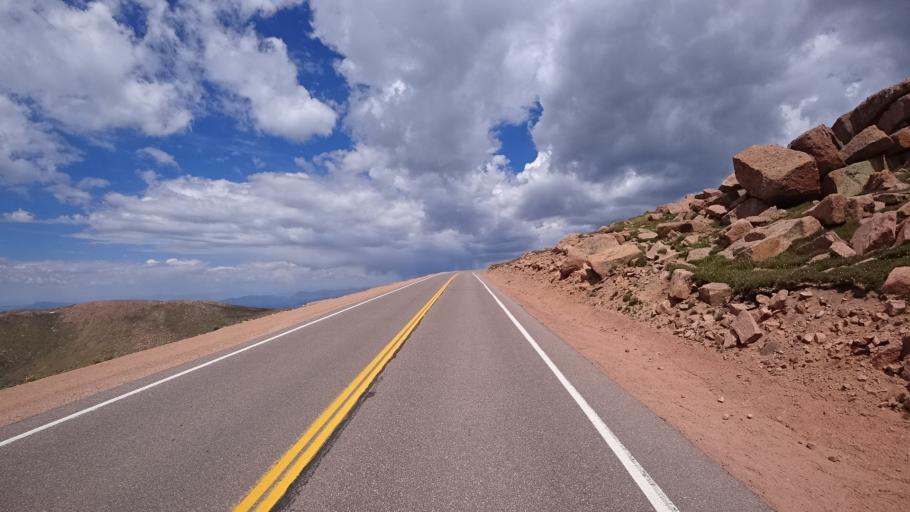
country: US
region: Colorado
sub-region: El Paso County
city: Cascade-Chipita Park
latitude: 38.8584
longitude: -105.0671
